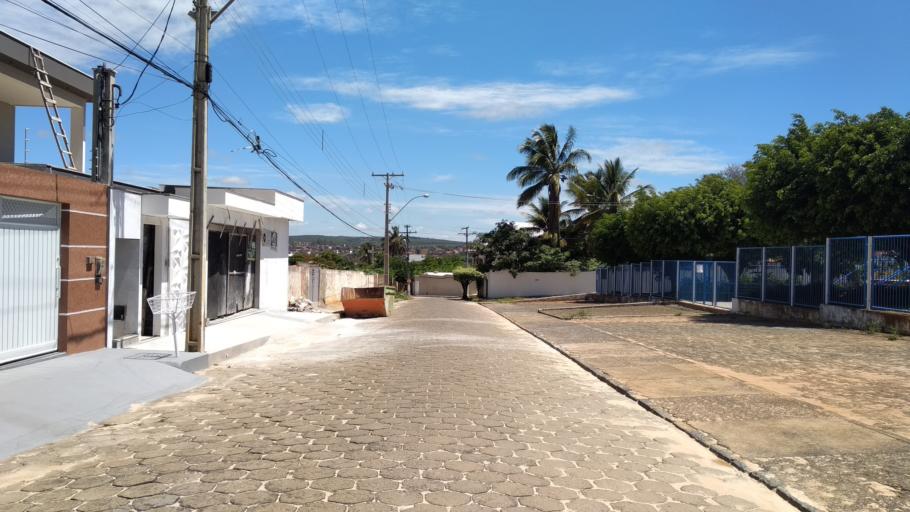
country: BR
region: Bahia
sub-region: Caetite
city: Caetite
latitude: -14.0717
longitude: -42.4819
